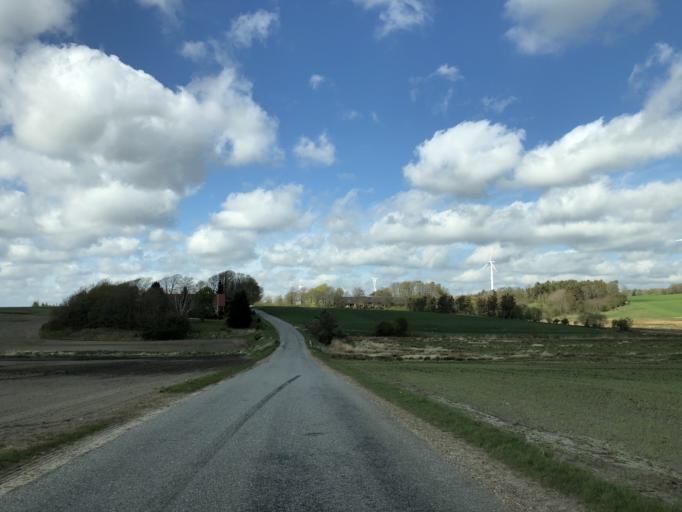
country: DK
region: Central Jutland
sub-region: Herning Kommune
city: Avlum
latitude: 56.2747
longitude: 8.6943
